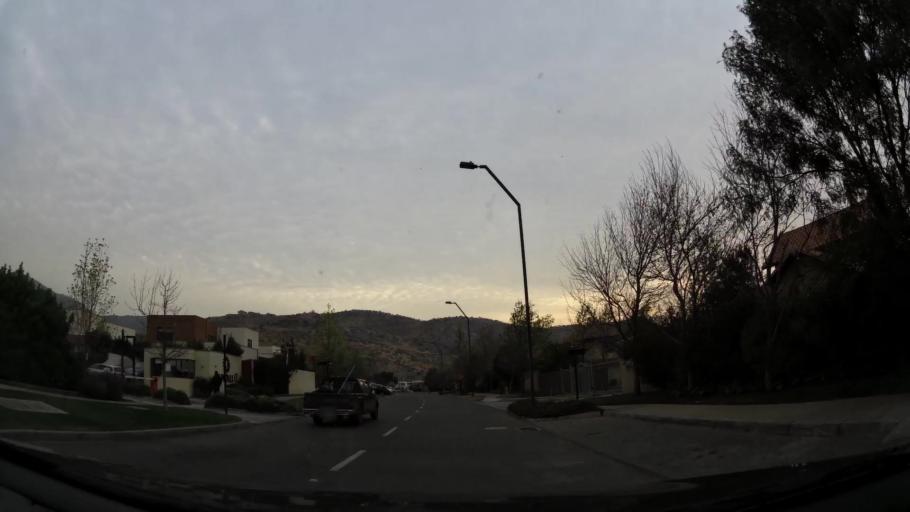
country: CL
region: Santiago Metropolitan
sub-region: Provincia de Chacabuco
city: Chicureo Abajo
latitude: -33.3101
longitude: -70.6562
